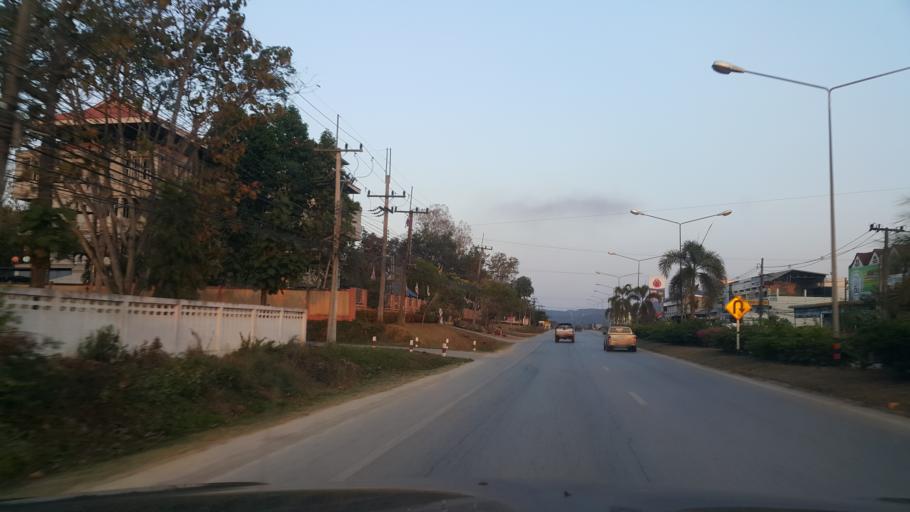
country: TH
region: Loei
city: Loei
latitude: 17.4937
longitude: 101.7084
